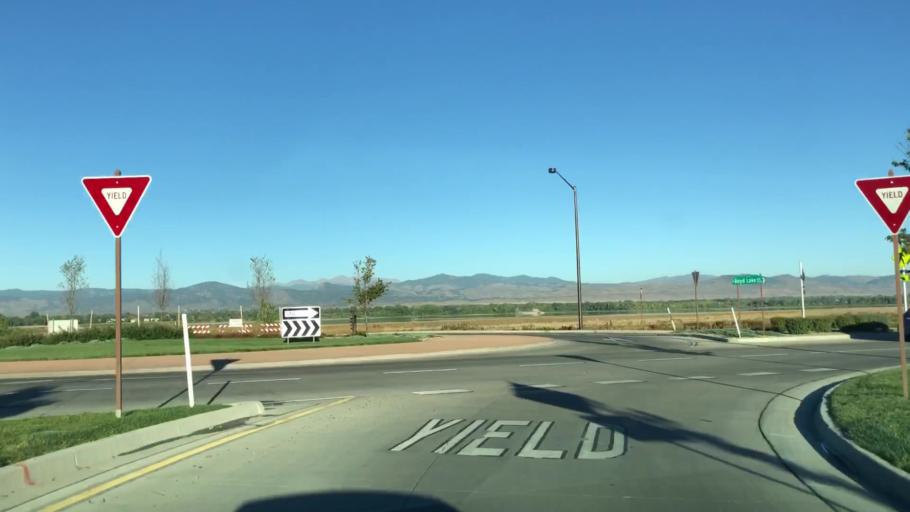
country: US
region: Colorado
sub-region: Larimer County
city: Loveland
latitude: 40.4145
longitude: -105.0205
